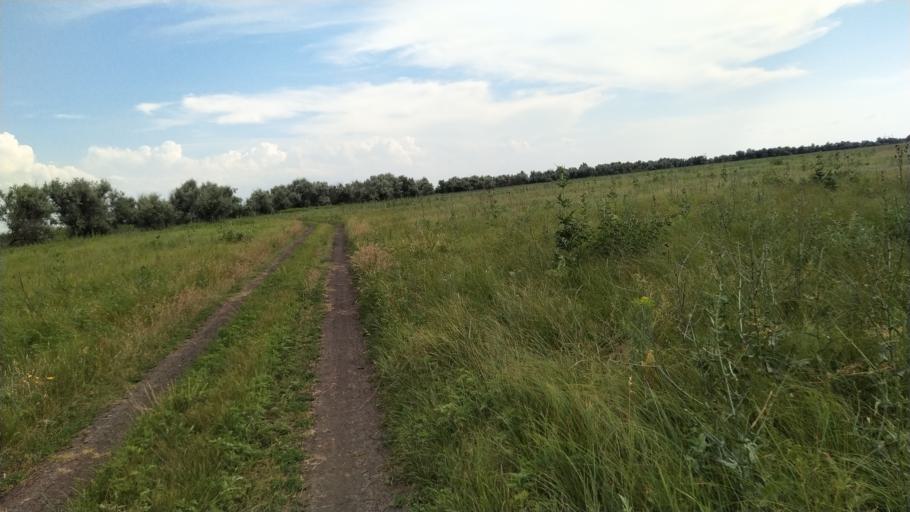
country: RU
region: Rostov
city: Kuleshovka
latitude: 47.1266
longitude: 39.6289
